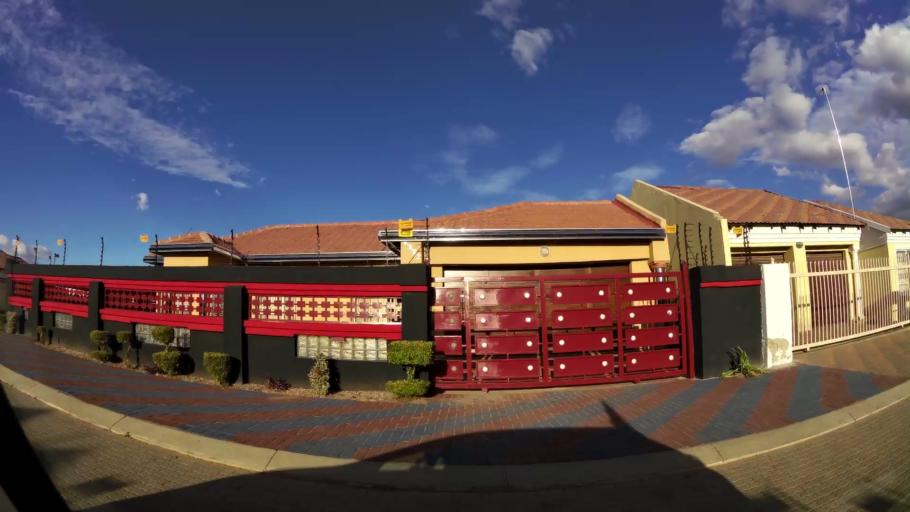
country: ZA
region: Limpopo
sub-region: Capricorn District Municipality
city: Polokwane
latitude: -23.9221
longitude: 29.4190
